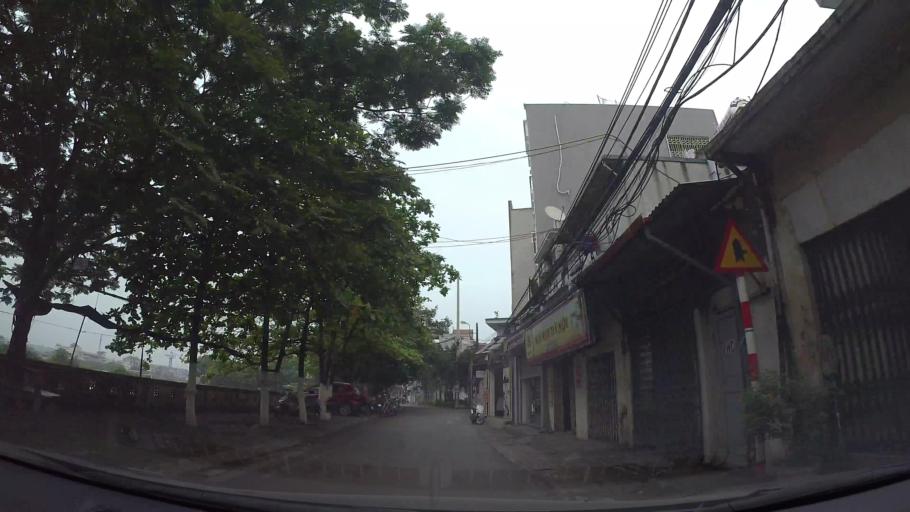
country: VN
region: Ha Noi
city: Van Dien
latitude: 20.9696
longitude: 105.8708
